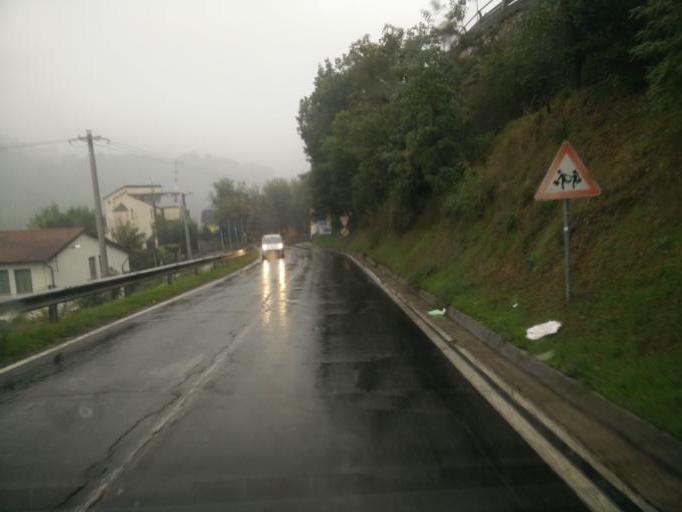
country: IT
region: Emilia-Romagna
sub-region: Provincia di Bologna
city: Grizzana
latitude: 44.2761
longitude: 11.2007
